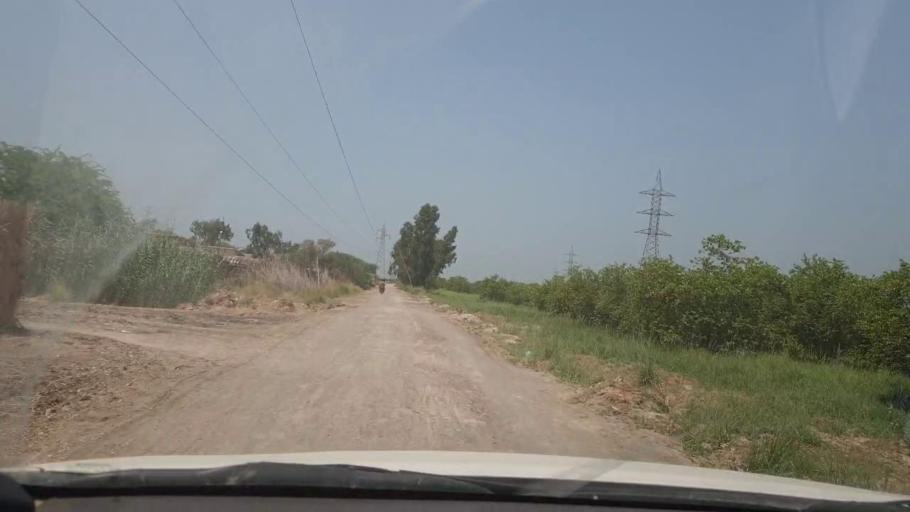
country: PK
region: Sindh
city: Lakhi
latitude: 27.8610
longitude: 68.6990
